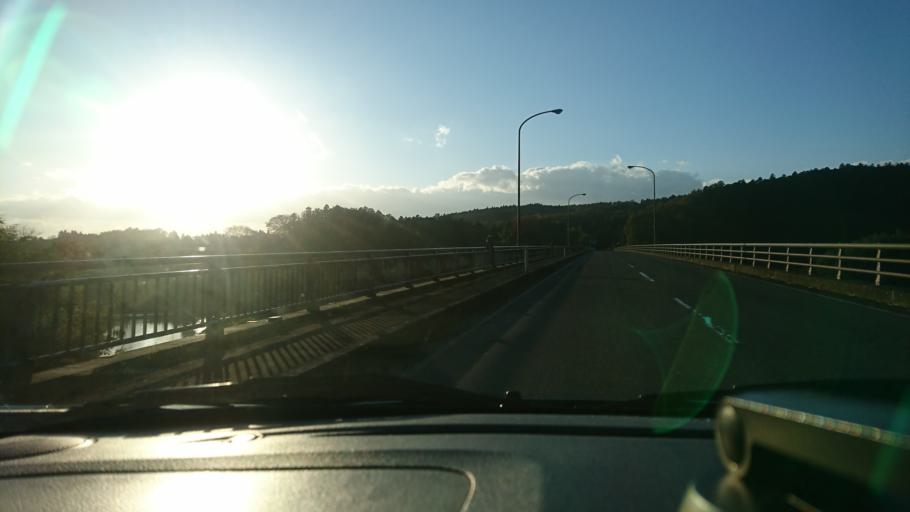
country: JP
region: Iwate
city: Ichinoseki
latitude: 38.7948
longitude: 141.2489
